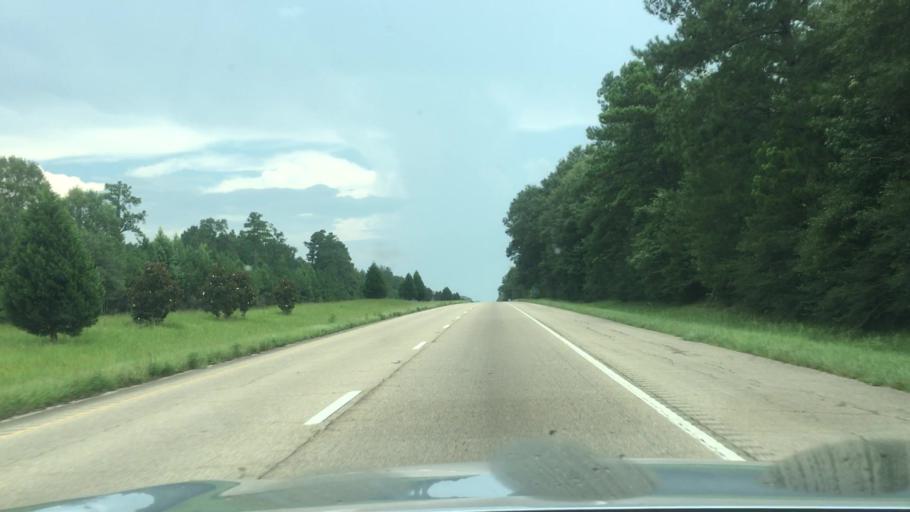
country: US
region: Mississippi
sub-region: Lamar County
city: Lumberton
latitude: 31.0044
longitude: -89.4166
